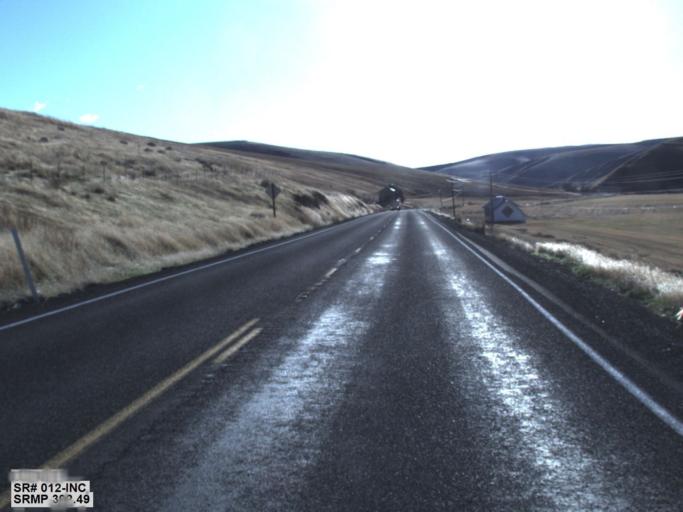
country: US
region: Washington
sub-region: Garfield County
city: Pomeroy
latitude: 46.5159
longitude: -117.7907
